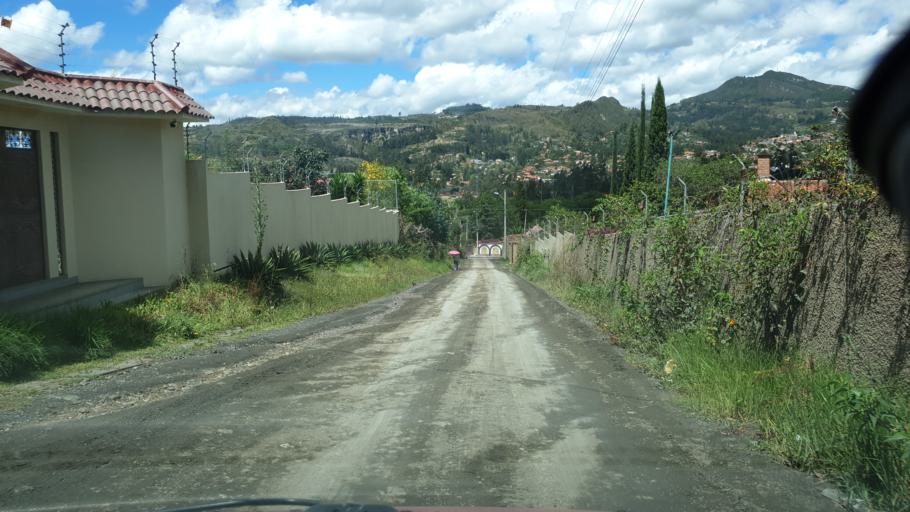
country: EC
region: Azuay
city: Llacao
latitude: -2.8431
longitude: -78.9039
